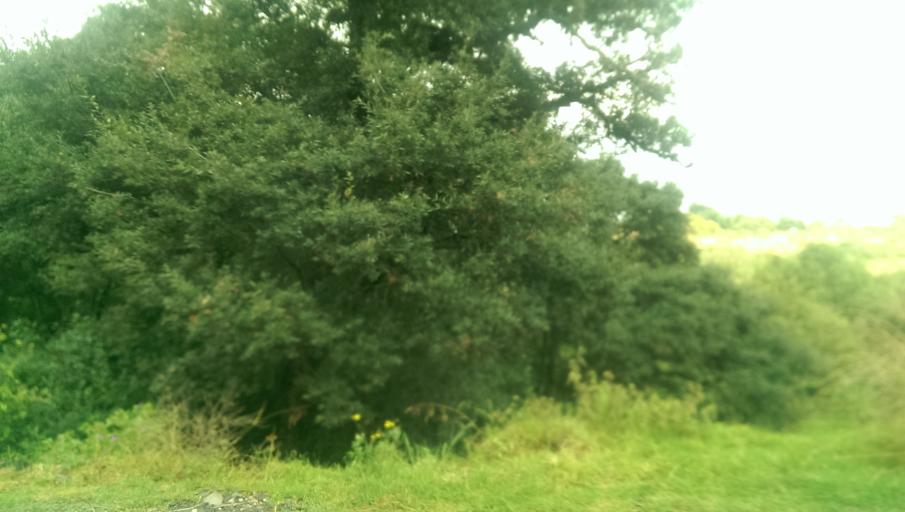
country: MX
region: Mexico
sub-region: Jilotepec
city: Jilotepec de Molina Enriquez
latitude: 19.9599
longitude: -99.4884
